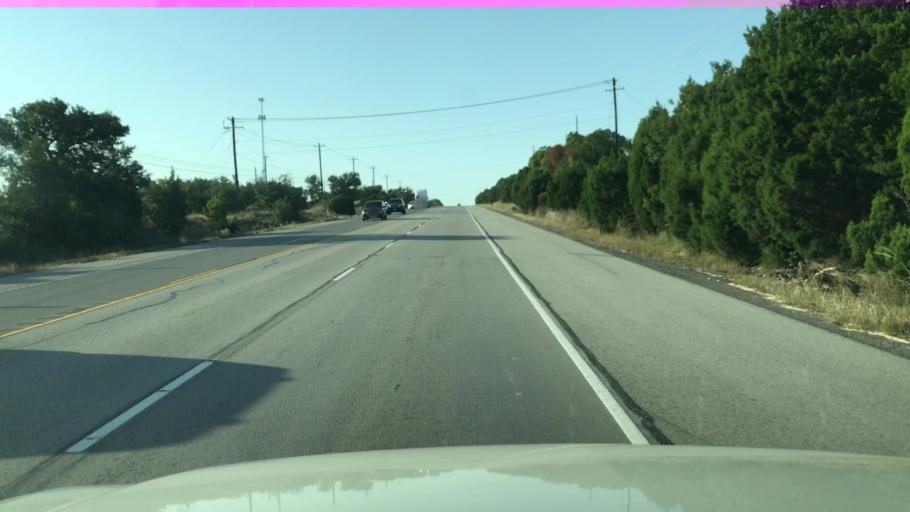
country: US
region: Texas
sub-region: Blanco County
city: Blanco
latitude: 30.1802
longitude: -98.3796
